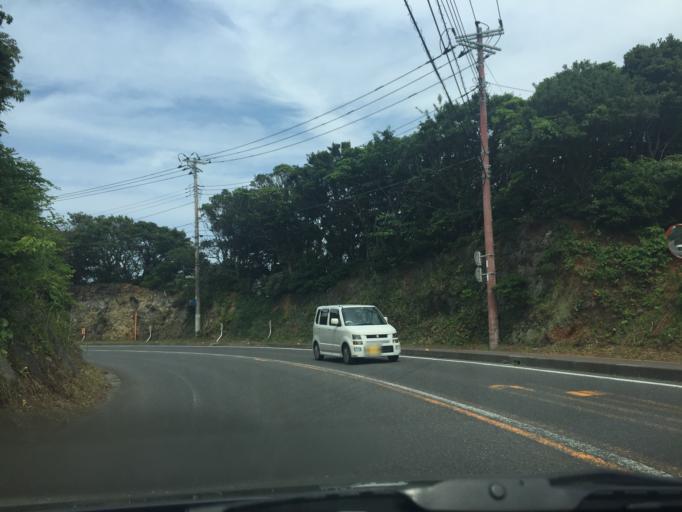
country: JP
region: Shizuoka
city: Shimoda
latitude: 34.6800
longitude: 138.9772
